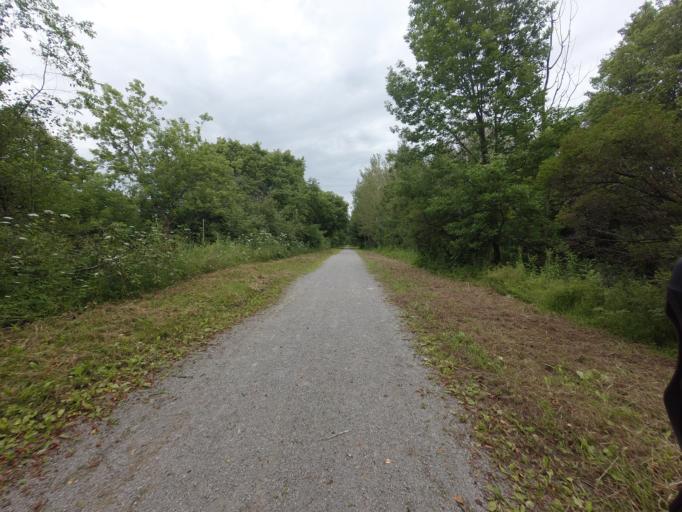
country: CA
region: Ontario
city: Bells Corners
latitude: 45.1366
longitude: -75.6099
